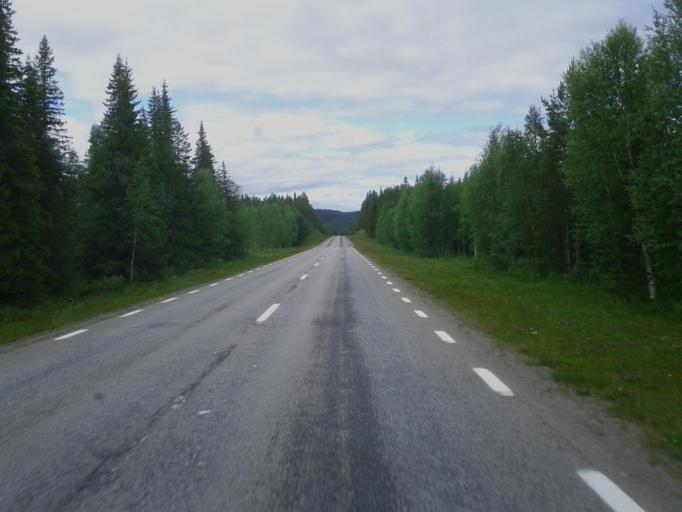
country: SE
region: Vaesterbotten
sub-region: Storumans Kommun
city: Fristad
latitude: 65.3571
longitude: 16.5547
